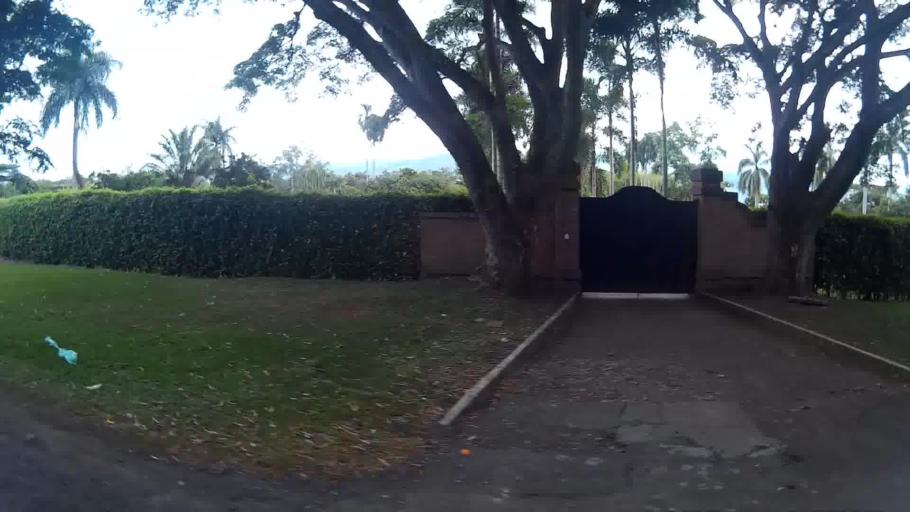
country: CO
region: Risaralda
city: La Virginia
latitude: 4.9308
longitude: -75.8630
